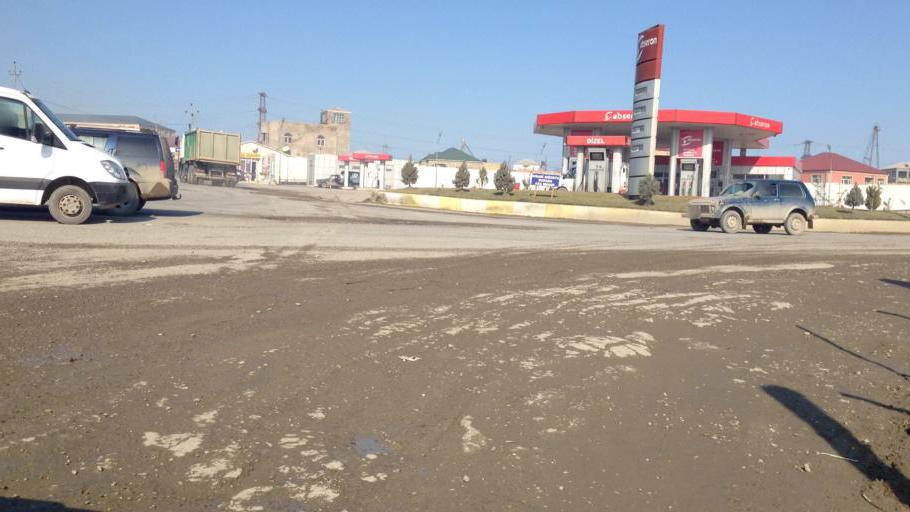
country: AZ
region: Abseron
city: Digah
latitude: 40.4802
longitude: 49.8558
